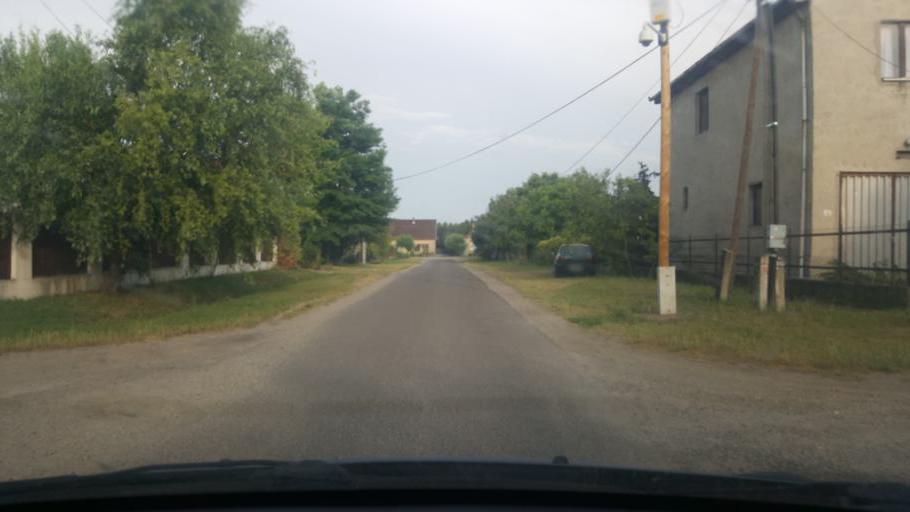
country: HU
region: Pest
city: Monor
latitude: 47.3343
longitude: 19.4457
